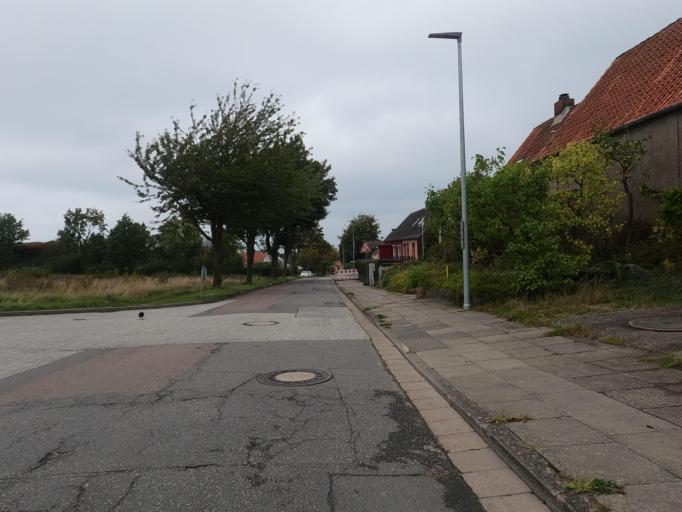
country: DE
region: Schleswig-Holstein
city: Heiligenhafen
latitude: 54.3644
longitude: 10.9847
